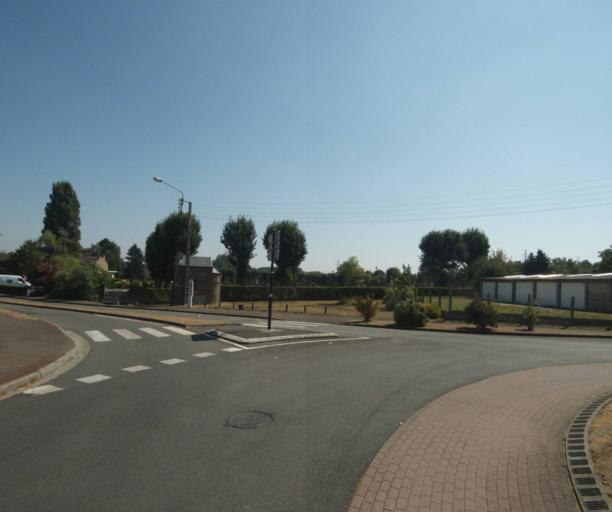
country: FR
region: Nord-Pas-de-Calais
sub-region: Departement du Nord
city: Bousbecque
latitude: 50.7658
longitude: 3.0772
